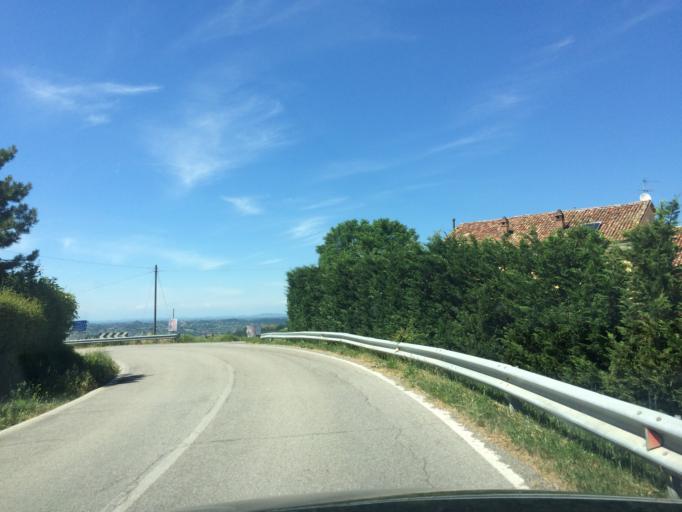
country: IT
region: Piedmont
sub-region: Provincia di Asti
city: Castel Boglione
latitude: 44.7309
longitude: 8.3963
